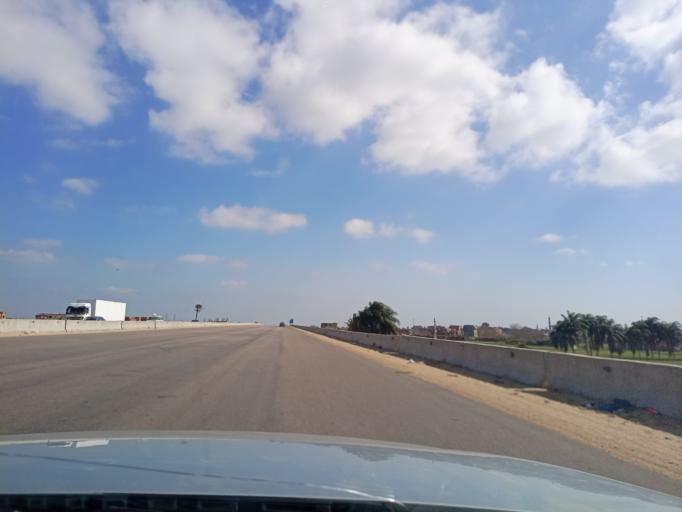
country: EG
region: Muhafazat al Minufiyah
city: Al Bajur
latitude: 30.4002
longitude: 31.0240
